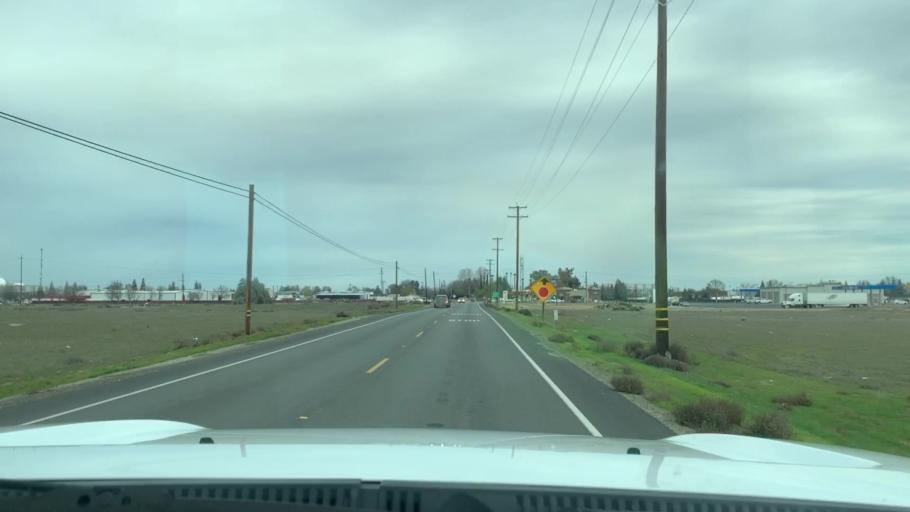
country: US
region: California
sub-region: Kern County
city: Shafter
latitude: 35.4387
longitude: -119.2518
